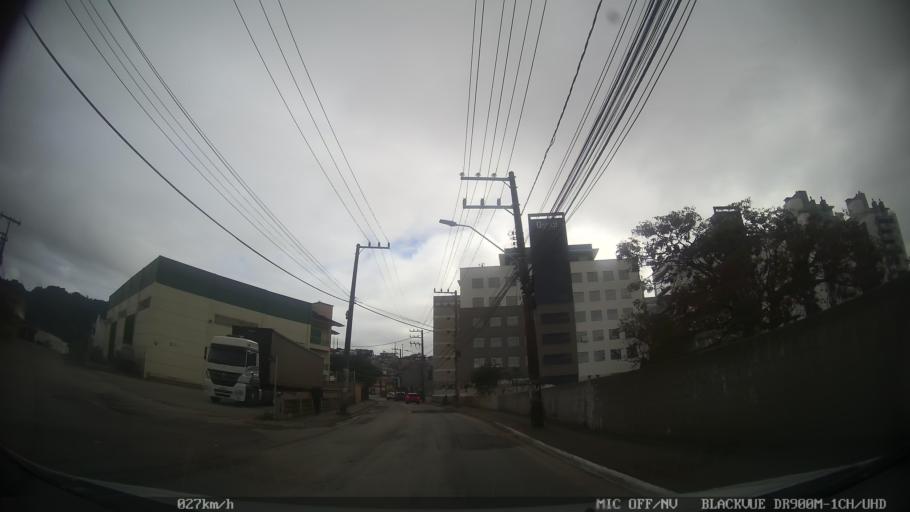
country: BR
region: Santa Catarina
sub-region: Sao Jose
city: Campinas
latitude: -27.5909
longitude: -48.6207
